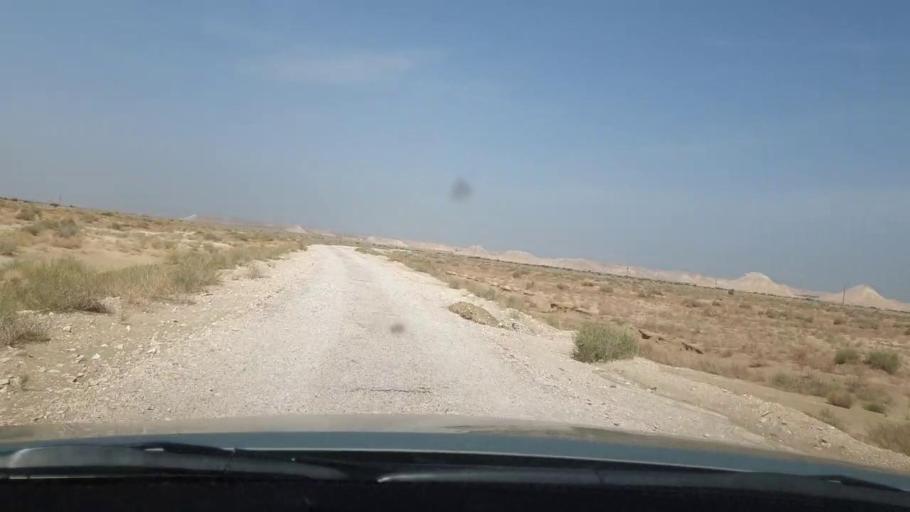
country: PK
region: Sindh
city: Kot Diji
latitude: 27.3274
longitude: 68.8070
